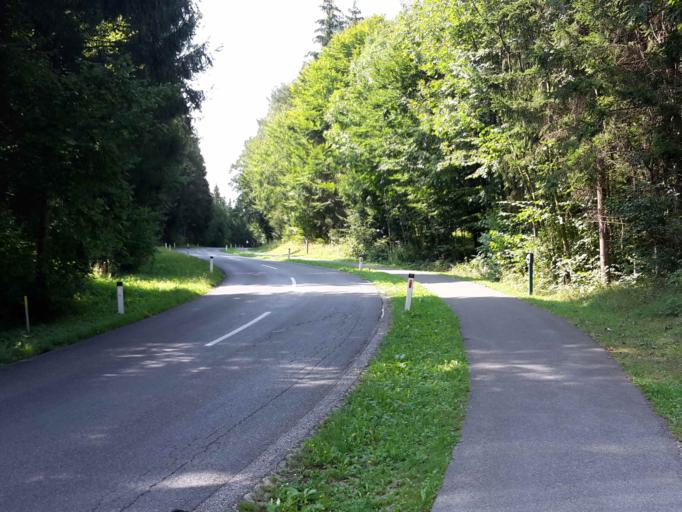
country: AT
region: Carinthia
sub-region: Politischer Bezirk Volkermarkt
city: Sittersdorf
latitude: 46.6003
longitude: 14.5706
